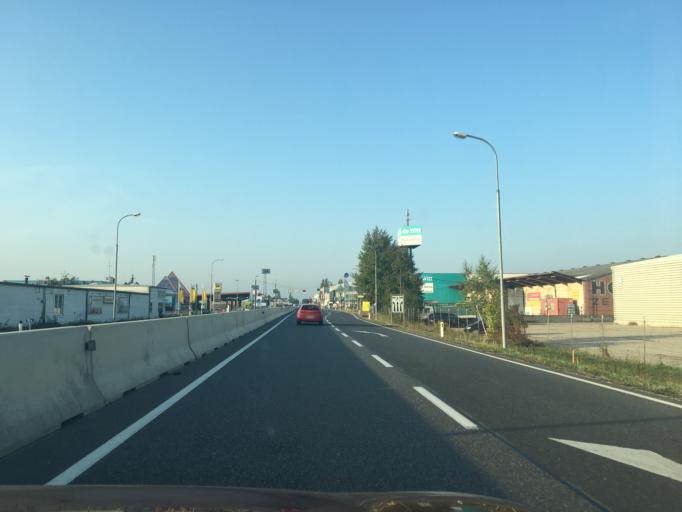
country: AT
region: Lower Austria
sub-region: Politischer Bezirk Mistelbach
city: Grossebersdorf
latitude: 48.3401
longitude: 16.4656
